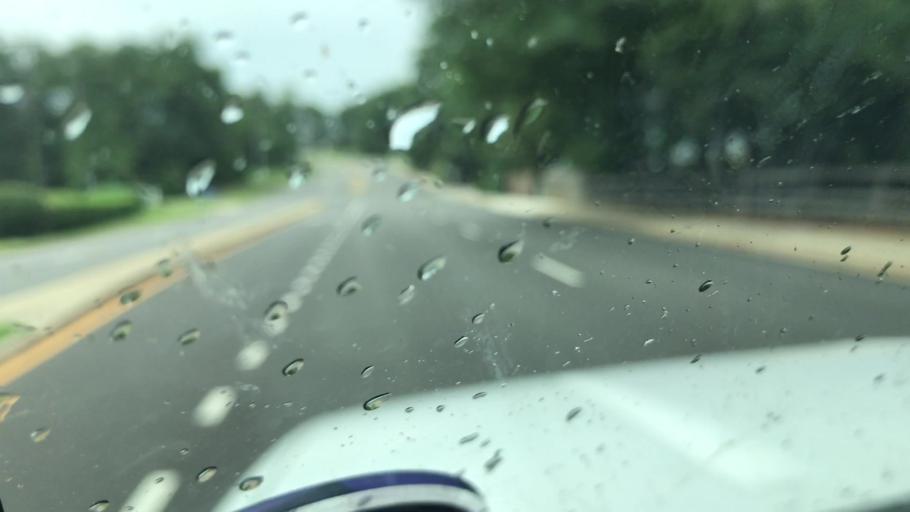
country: US
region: Virginia
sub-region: Henrico County
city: Short Pump
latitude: 37.6272
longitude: -77.6093
